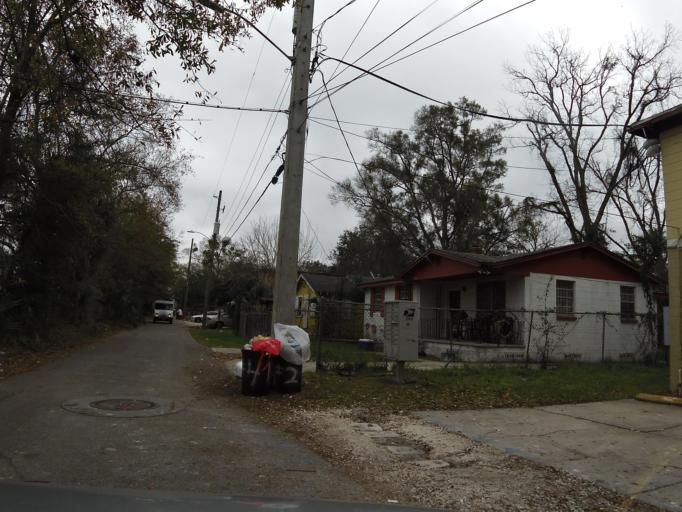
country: US
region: Florida
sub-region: Duval County
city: Jacksonville
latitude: 30.3520
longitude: -81.6875
